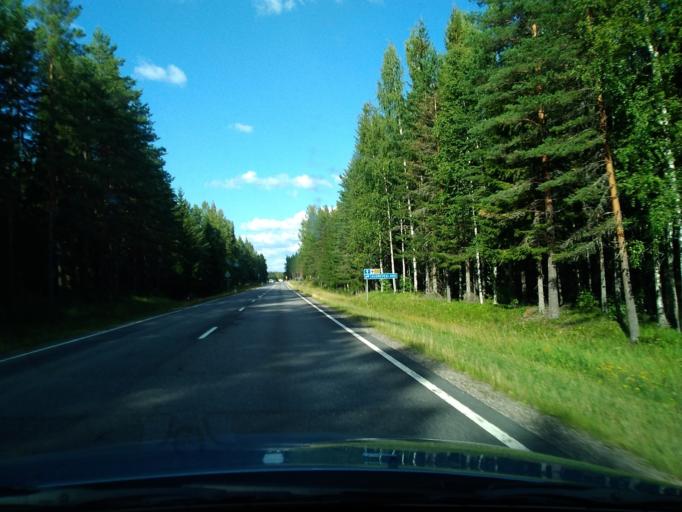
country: FI
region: Pirkanmaa
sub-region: Ylae-Pirkanmaa
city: Maenttae
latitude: 61.9694
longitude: 24.5996
